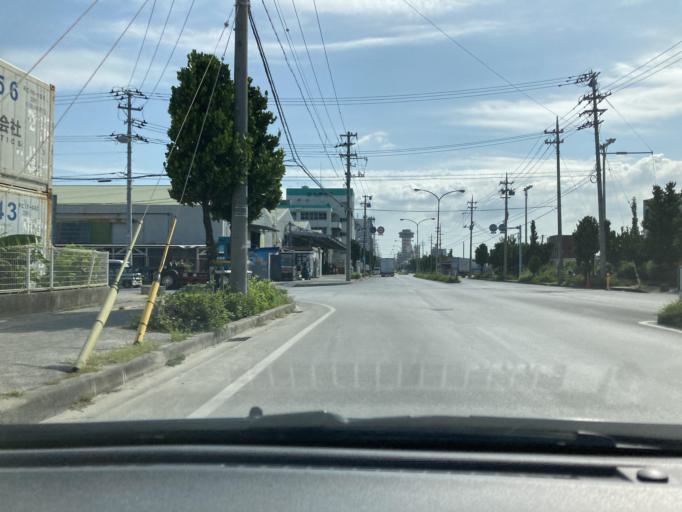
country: JP
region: Okinawa
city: Naha-shi
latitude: 26.2413
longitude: 127.6729
